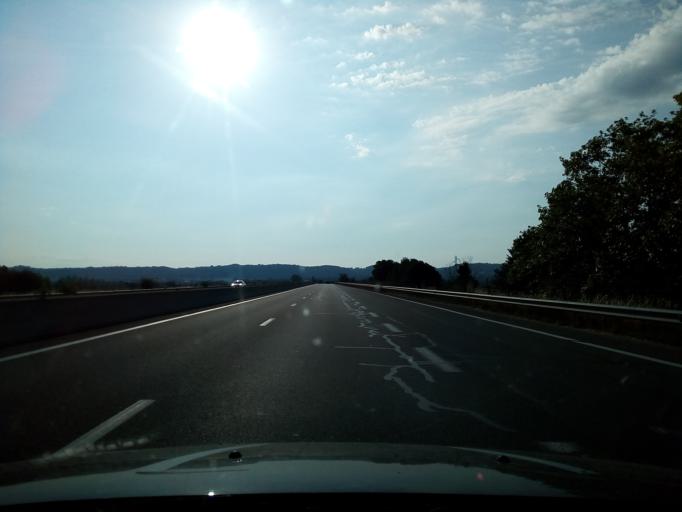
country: FR
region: Auvergne
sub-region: Departement de l'Allier
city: Saint-Victor
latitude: 46.3761
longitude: 2.5881
